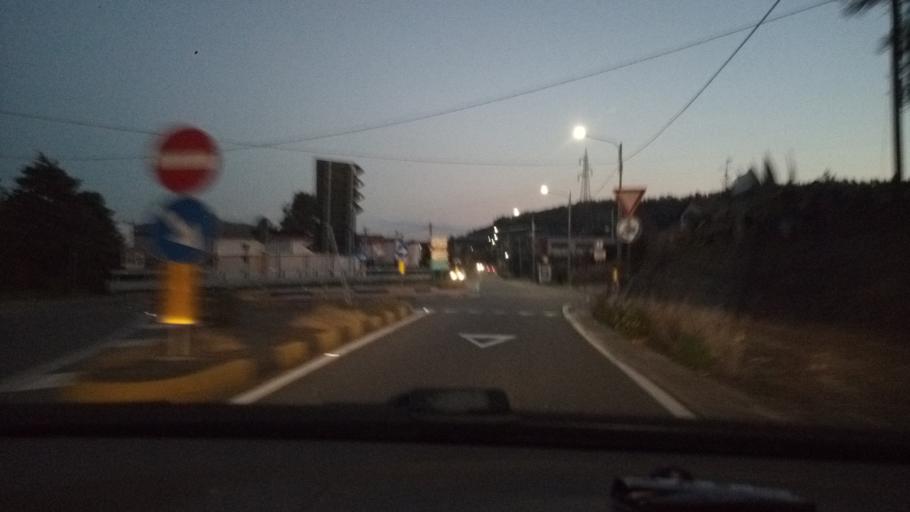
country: IT
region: Calabria
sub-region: Provincia di Catanzaro
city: Cava-Cuculera Nobile
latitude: 38.8862
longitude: 16.6230
